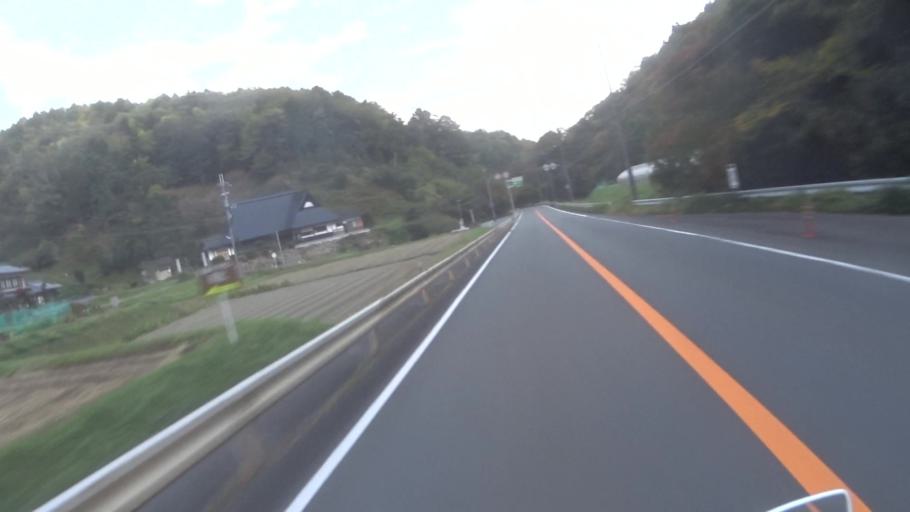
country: JP
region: Kyoto
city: Ayabe
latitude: 35.2305
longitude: 135.3343
